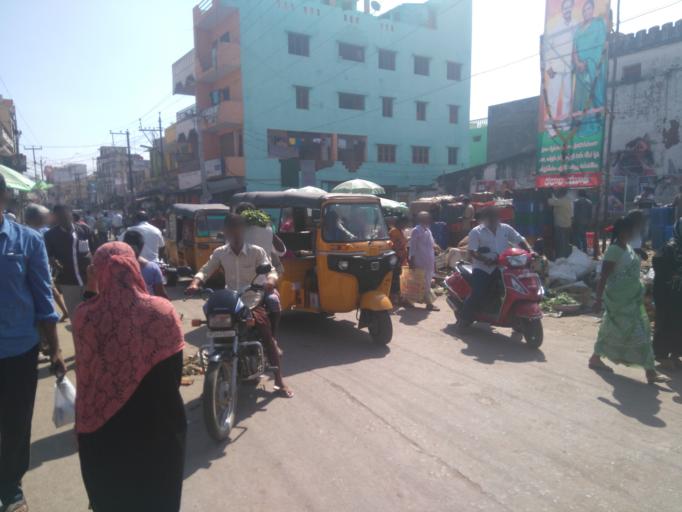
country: IN
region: Andhra Pradesh
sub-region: Chittoor
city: Chittoor
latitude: 13.2172
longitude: 79.0943
